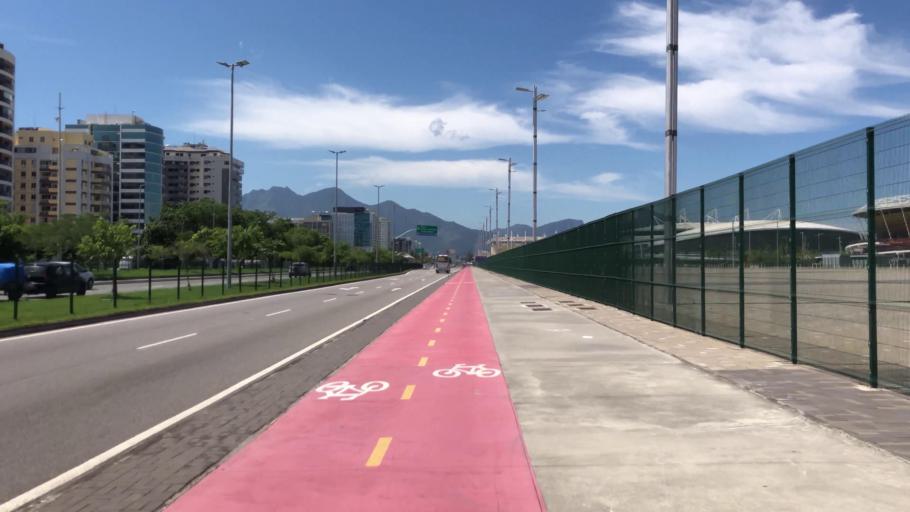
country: BR
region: Rio de Janeiro
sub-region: Nilopolis
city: Nilopolis
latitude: -22.9897
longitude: -43.4174
